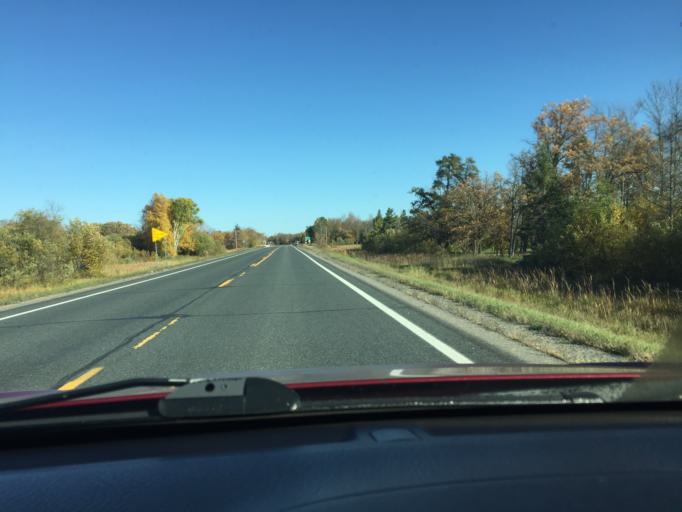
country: US
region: Minnesota
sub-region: Beltrami County
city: Redby
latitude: 48.1731
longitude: -94.5128
